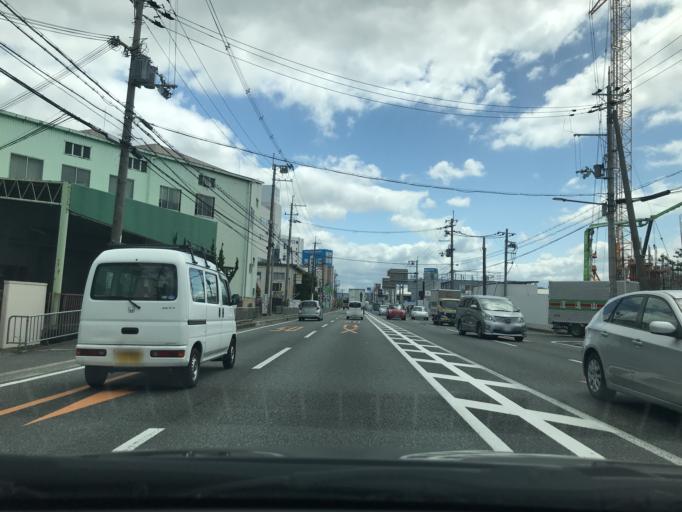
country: JP
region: Osaka
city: Ibaraki
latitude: 34.8352
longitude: 135.5564
